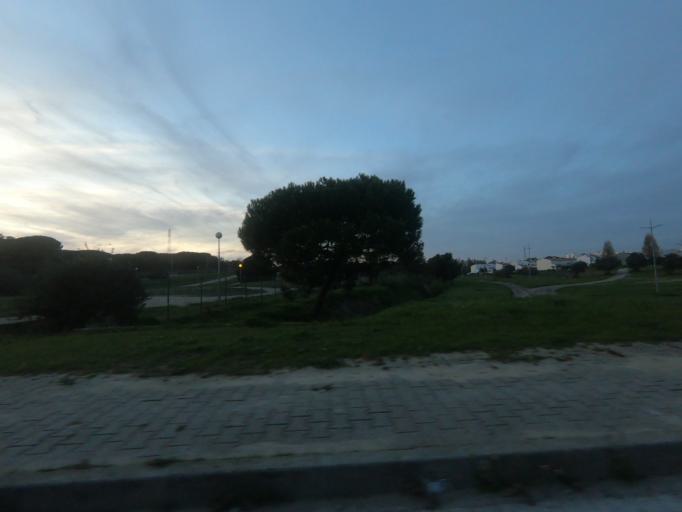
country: PT
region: Setubal
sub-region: Setubal
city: Setubal
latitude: 38.5185
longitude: -8.8502
